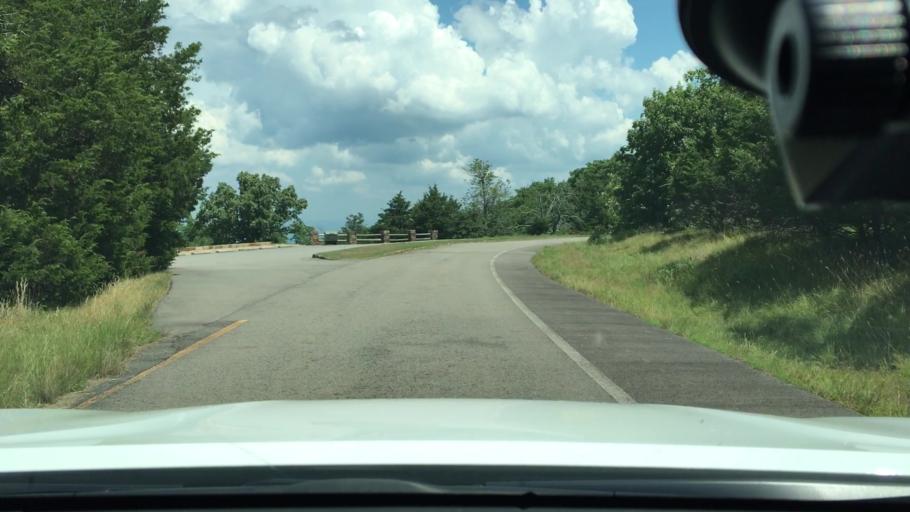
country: US
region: Arkansas
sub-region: Logan County
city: Paris
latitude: 35.1719
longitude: -93.6475
